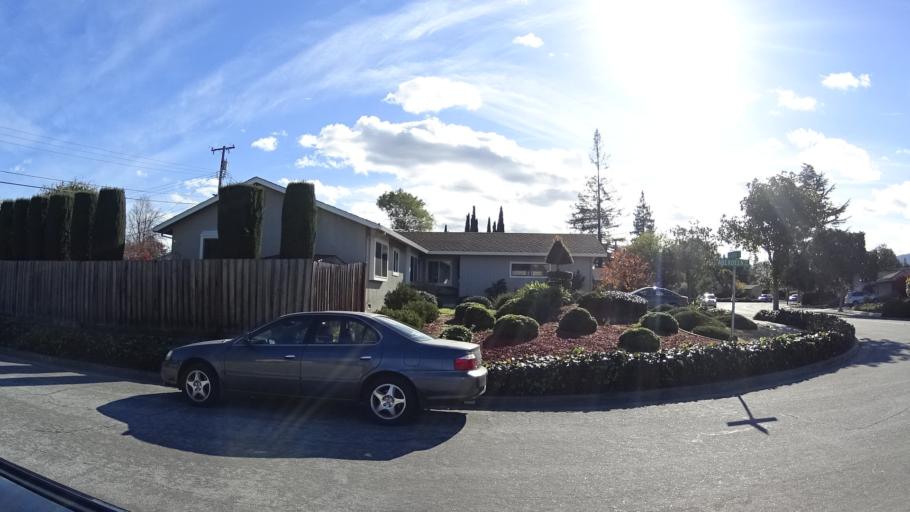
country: US
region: California
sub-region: Santa Clara County
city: Sunnyvale
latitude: 37.3516
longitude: -122.0530
